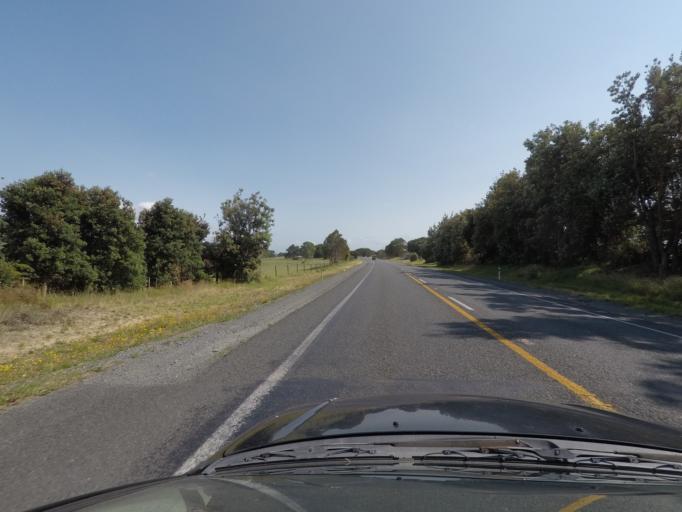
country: NZ
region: Northland
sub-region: Whangarei
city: Ruakaka
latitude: -35.9443
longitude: 174.4555
